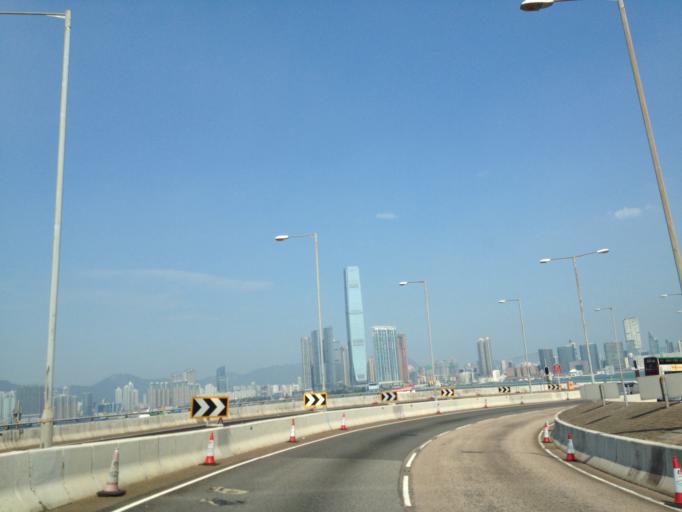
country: HK
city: Hong Kong
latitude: 22.2898
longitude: 114.1405
